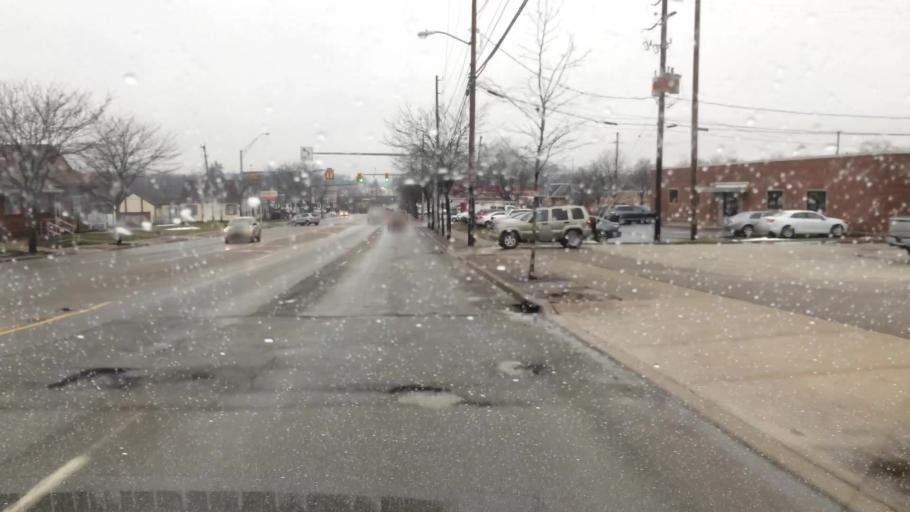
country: US
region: Ohio
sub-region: Summit County
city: Cuyahoga Falls
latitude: 41.1022
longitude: -81.4790
